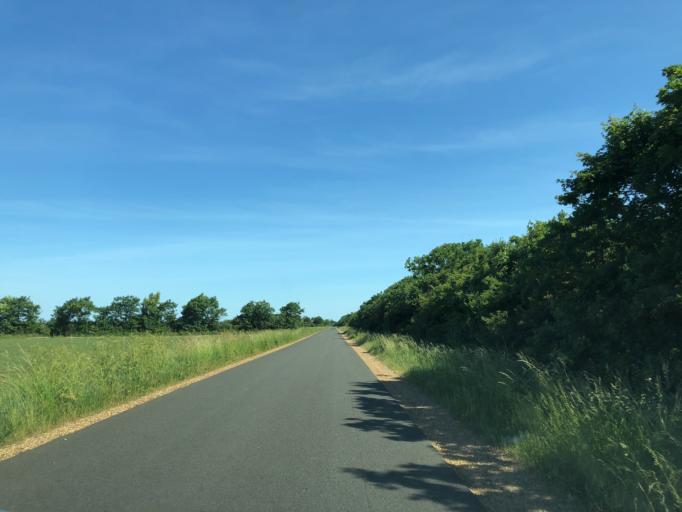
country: DK
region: Central Jutland
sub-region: Holstebro Kommune
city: Ulfborg
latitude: 56.3822
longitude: 8.4260
